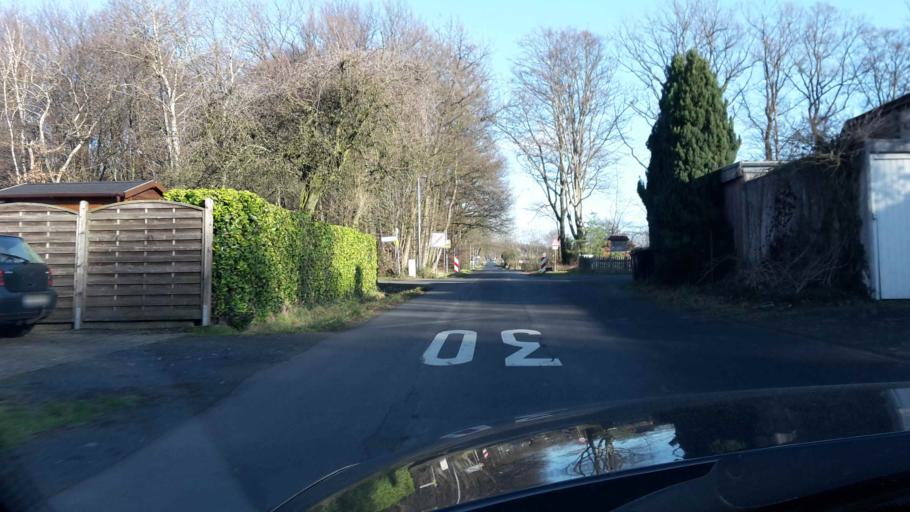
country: DE
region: North Rhine-Westphalia
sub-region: Regierungsbezirk Koln
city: Hennef
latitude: 50.7116
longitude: 7.2999
